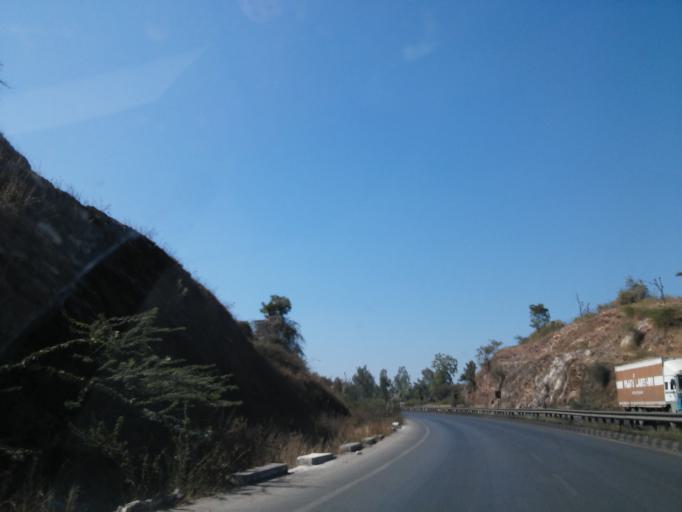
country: IN
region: Rajasthan
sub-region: Dungarpur
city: Dungarpur
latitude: 23.9075
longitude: 73.5498
